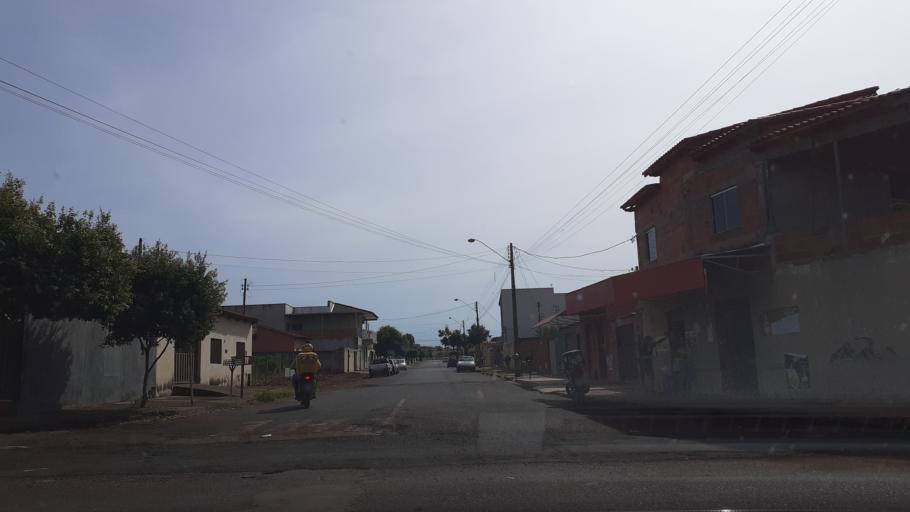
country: BR
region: Goias
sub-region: Itumbiara
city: Itumbiara
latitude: -18.4229
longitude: -49.2412
